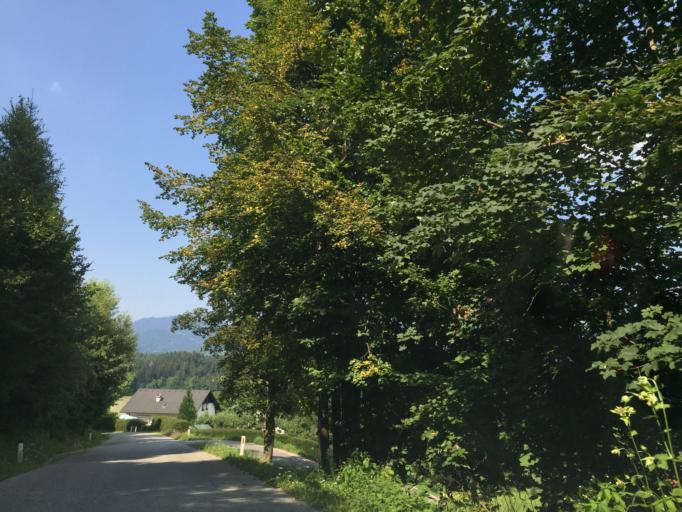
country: SI
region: Slovenj Gradec
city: Smartno pri Slovenj Gradcu
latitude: 46.4496
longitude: 15.1205
